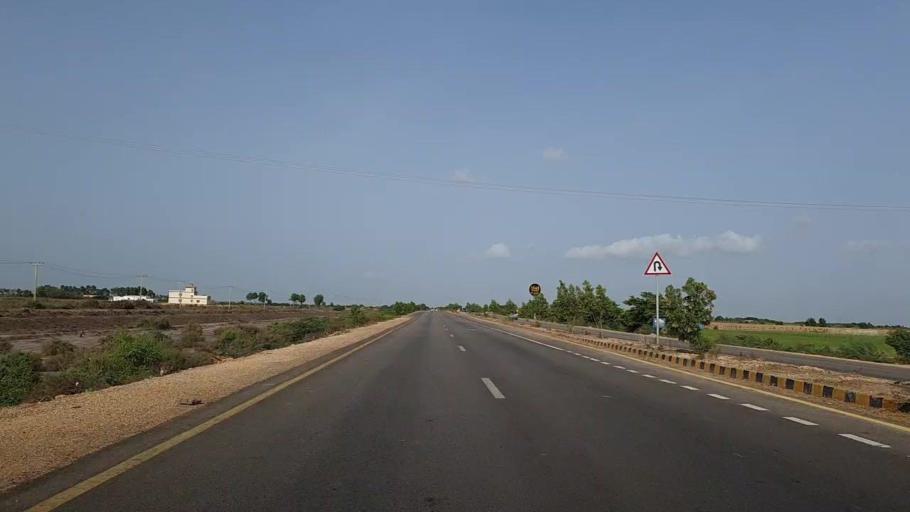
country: PK
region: Sindh
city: Thatta
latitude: 24.7422
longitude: 67.8169
